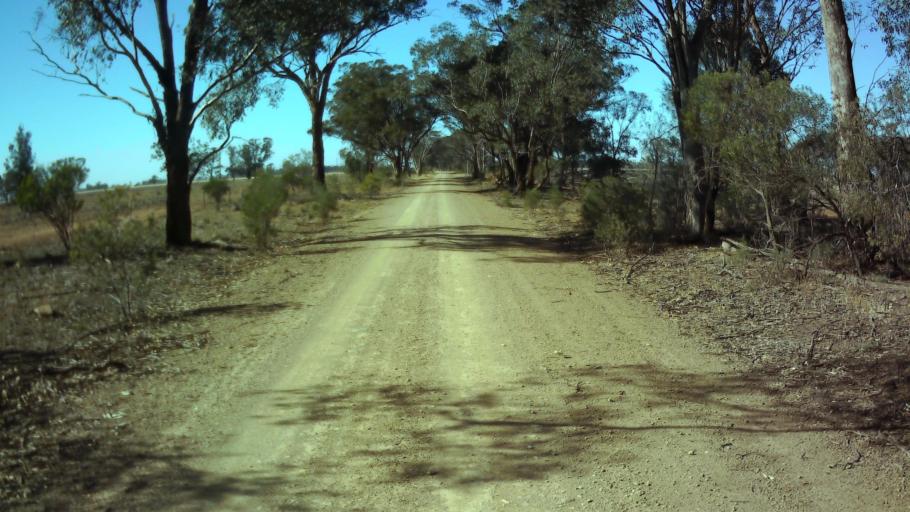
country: AU
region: New South Wales
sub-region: Weddin
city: Grenfell
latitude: -33.9417
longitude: 147.8708
